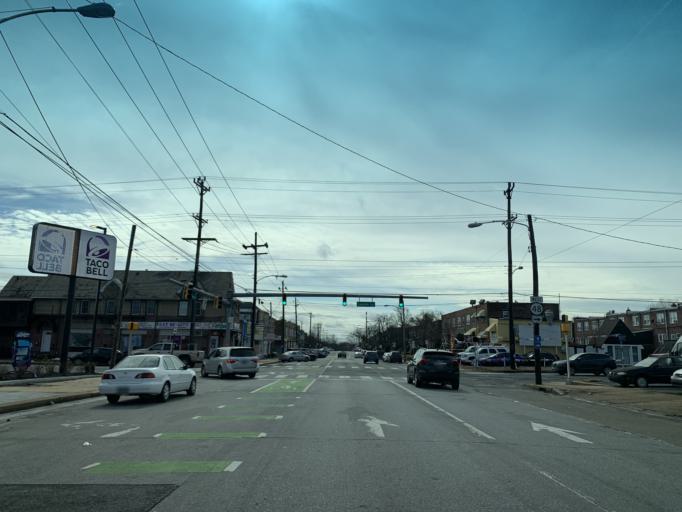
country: US
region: Delaware
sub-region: New Castle County
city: Elsmere
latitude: 39.7472
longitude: -75.5744
